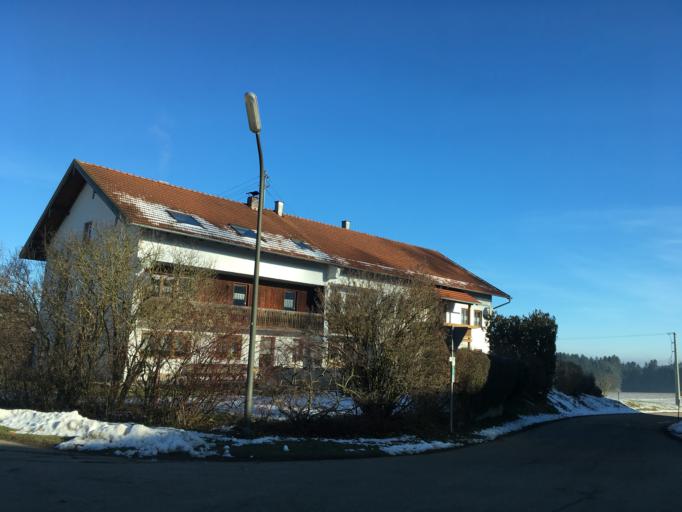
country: DE
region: Bavaria
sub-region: Upper Bavaria
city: Schnaitsee
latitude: 48.0916
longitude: 12.3624
